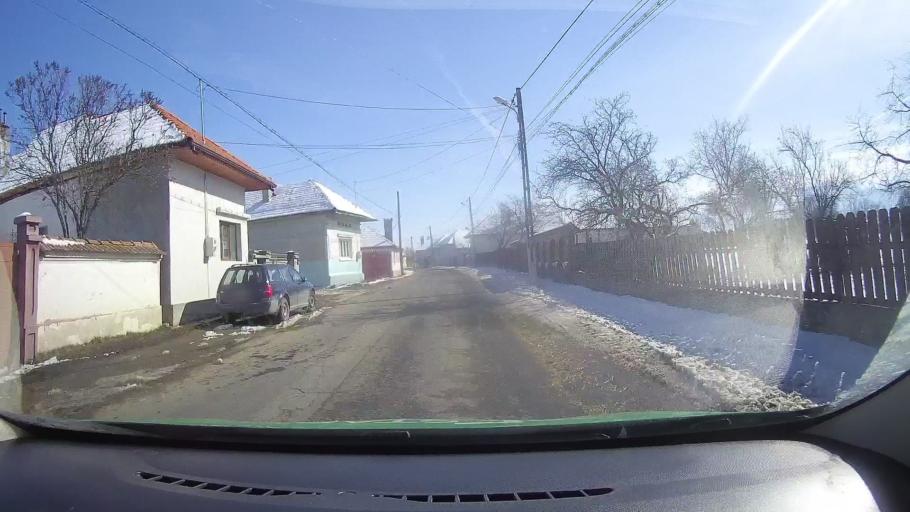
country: RO
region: Brasov
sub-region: Comuna Recea
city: Recea
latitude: 45.7316
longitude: 24.9458
